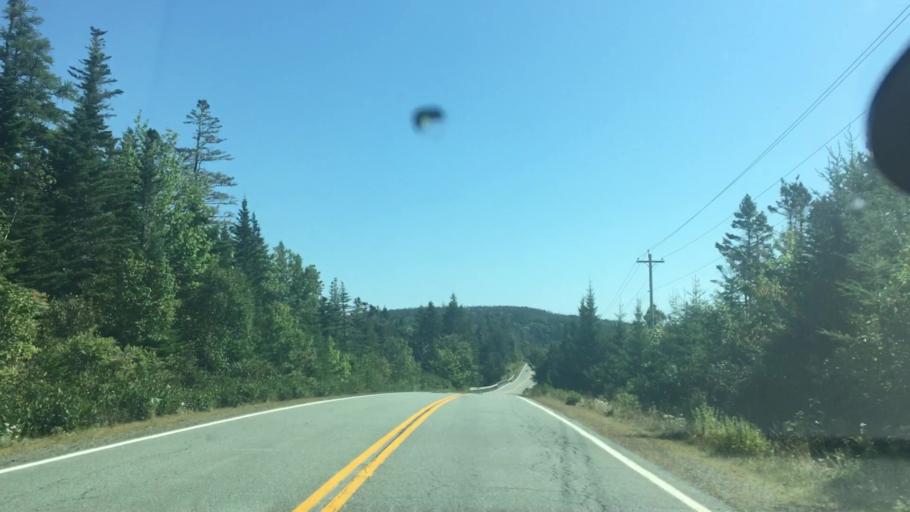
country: CA
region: Nova Scotia
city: Antigonish
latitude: 45.0133
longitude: -62.0997
